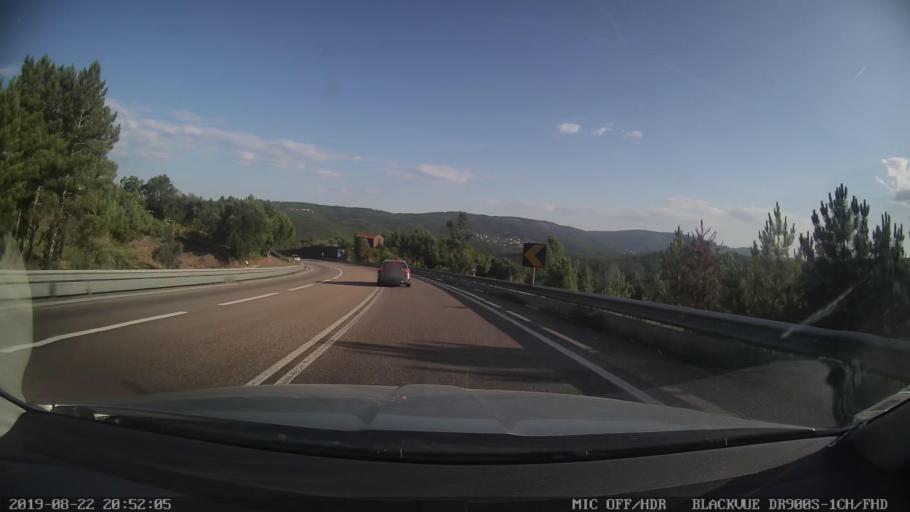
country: PT
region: Castelo Branco
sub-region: Proenca-A-Nova
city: Proenca-a-Nova
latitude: 39.7669
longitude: -7.9669
